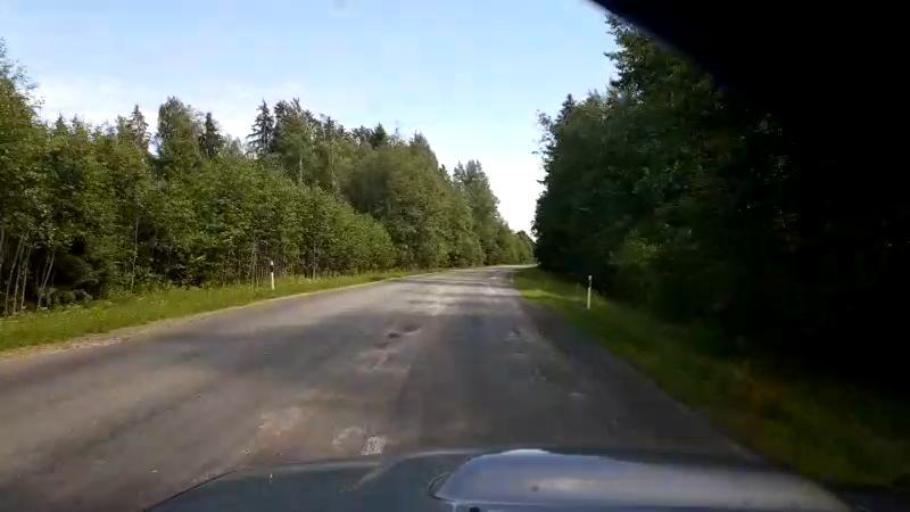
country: EE
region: Laeaene-Virumaa
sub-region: Rakke vald
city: Rakke
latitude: 58.9130
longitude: 26.2704
